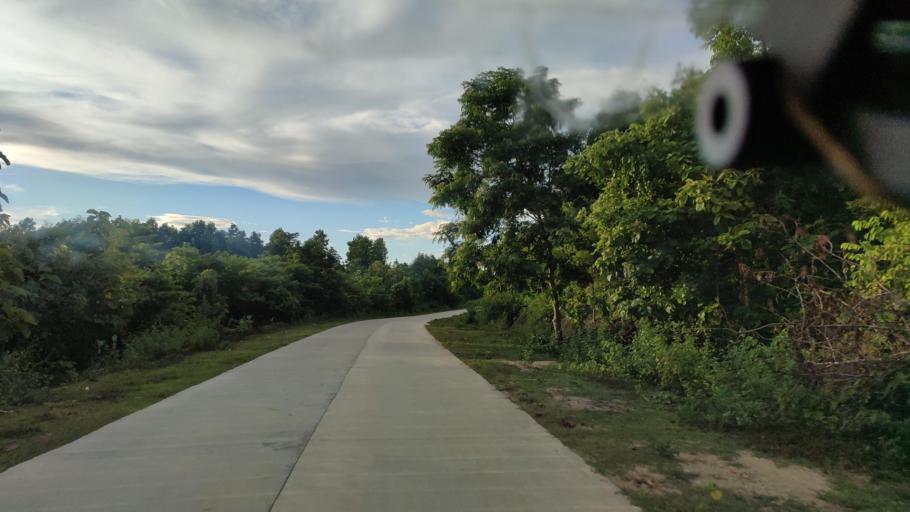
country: MM
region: Magway
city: Taungdwingyi
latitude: 20.0336
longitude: 95.7868
